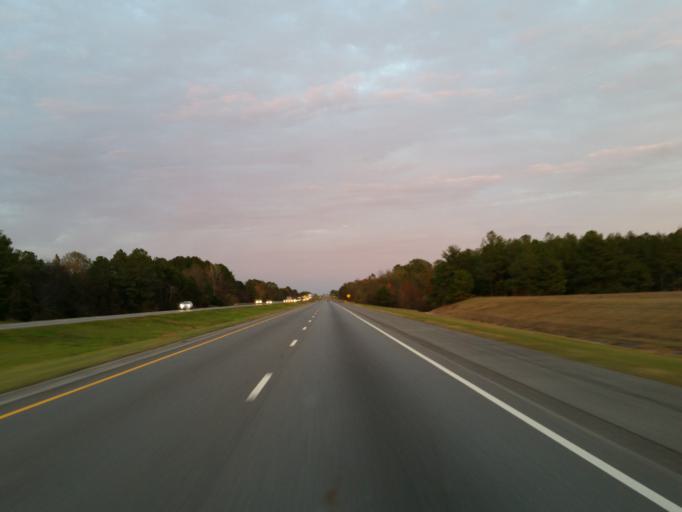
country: US
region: Alabama
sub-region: Sumter County
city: Livingston
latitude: 32.7277
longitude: -88.1109
